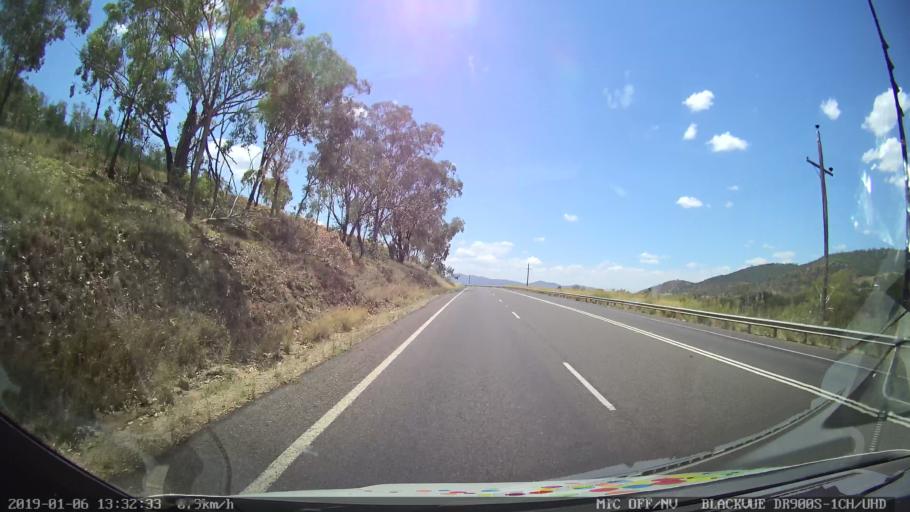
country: AU
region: New South Wales
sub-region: Tamworth Municipality
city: East Tamworth
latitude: -31.1089
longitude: 150.9993
